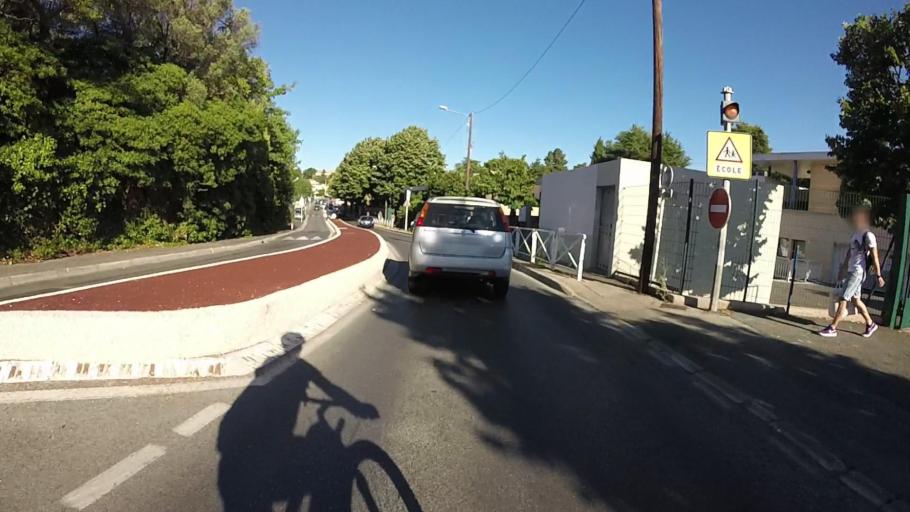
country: FR
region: Provence-Alpes-Cote d'Azur
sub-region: Departement des Alpes-Maritimes
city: Antibes
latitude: 43.5846
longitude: 7.1033
